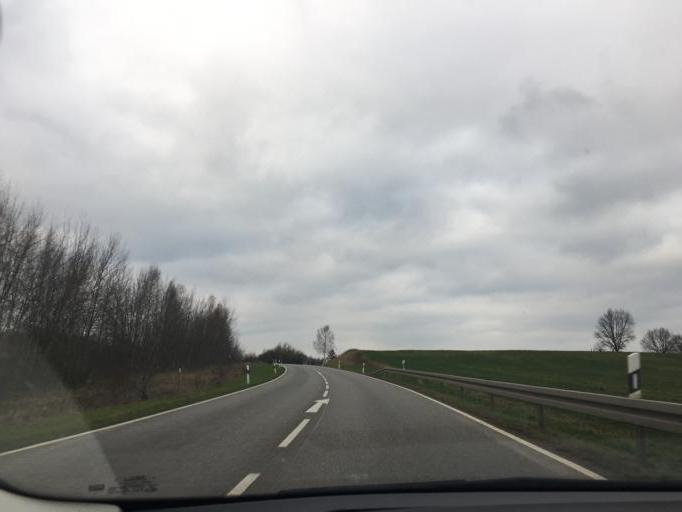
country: DE
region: Thuringia
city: Langenleuba-Niederhain
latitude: 50.9883
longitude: 12.6080
